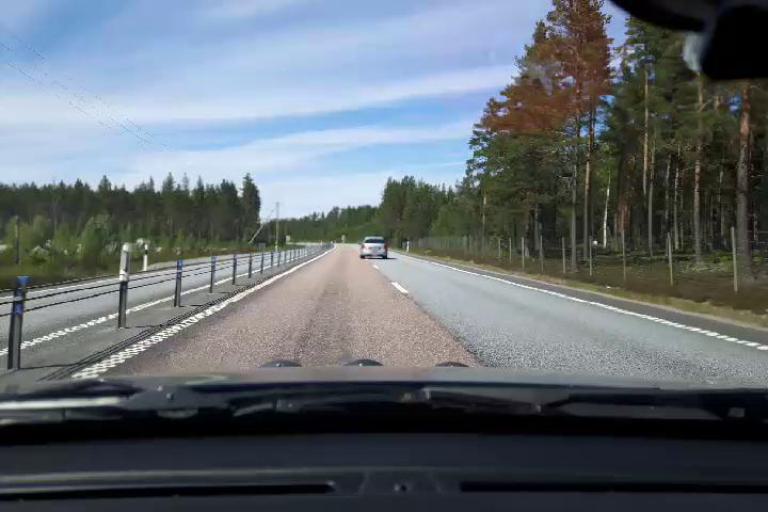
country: SE
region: Gaevleborg
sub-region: Gavle Kommun
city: Norrsundet
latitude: 61.0281
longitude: 16.9752
